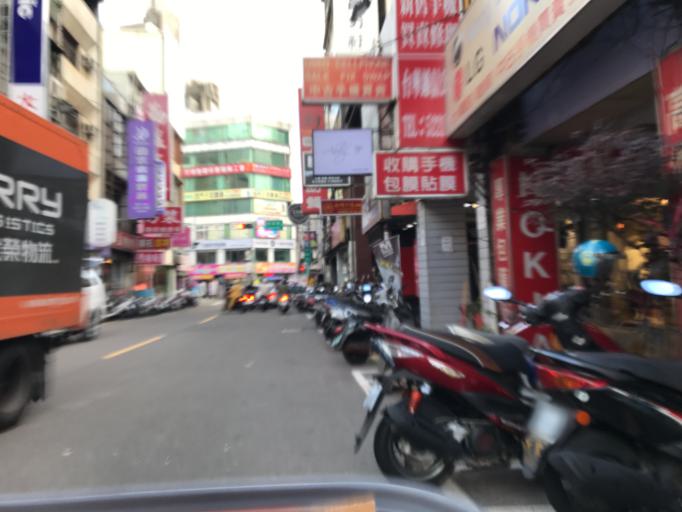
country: TW
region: Taiwan
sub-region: Hsinchu
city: Hsinchu
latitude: 24.8020
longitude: 120.9679
